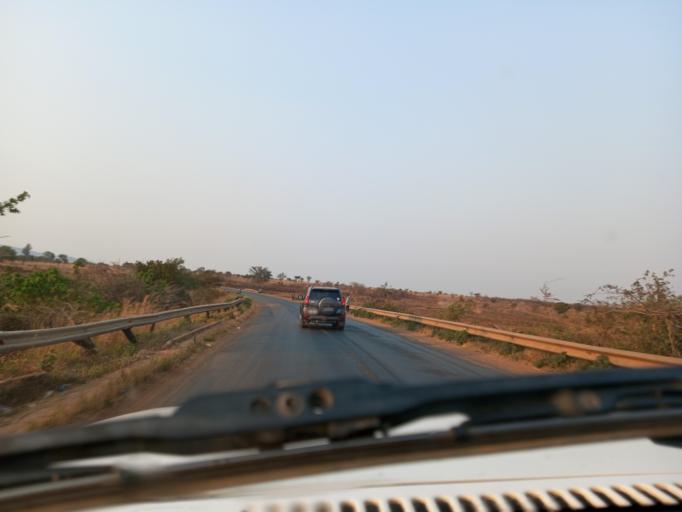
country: ZM
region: Northern
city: Mpika
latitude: -11.8999
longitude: 31.4140
